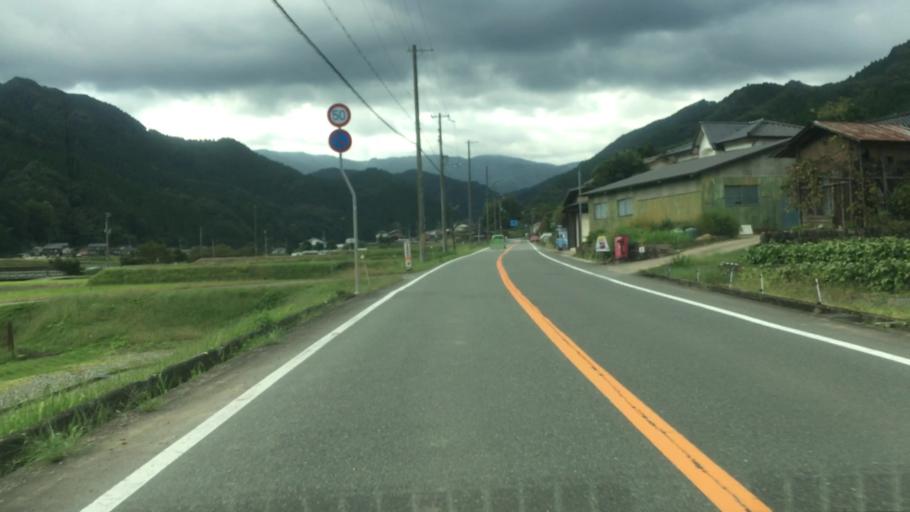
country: JP
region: Hyogo
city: Toyooka
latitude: 35.4110
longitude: 134.7386
